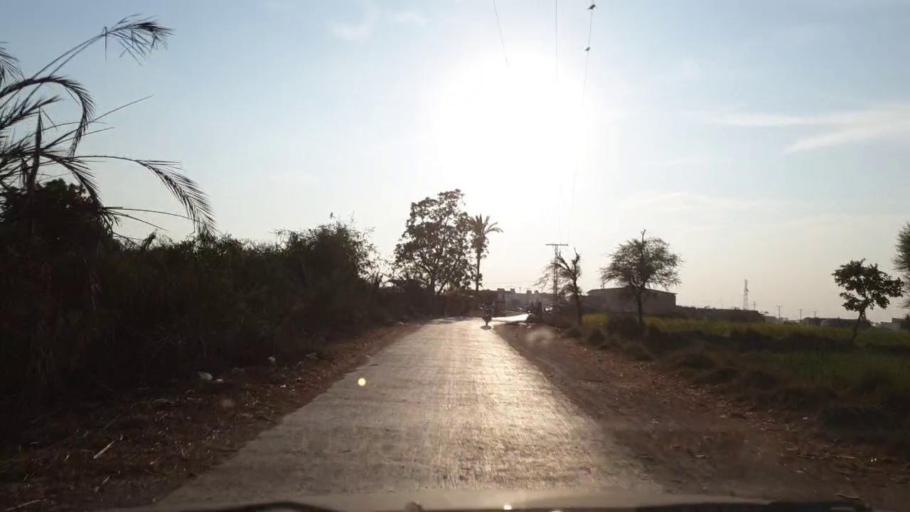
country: PK
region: Sindh
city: Khadro
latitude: 26.1515
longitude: 68.7209
